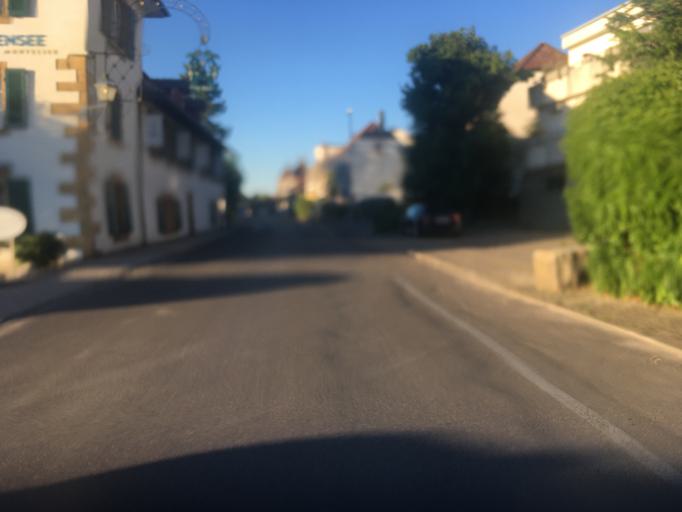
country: CH
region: Fribourg
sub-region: See District
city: Murten
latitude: 46.9341
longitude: 7.1221
